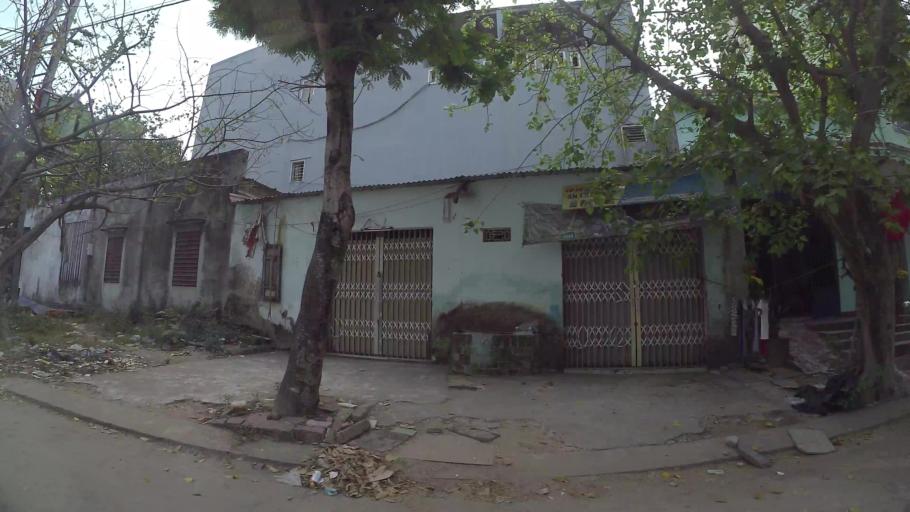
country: VN
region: Da Nang
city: Son Tra
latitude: 16.0890
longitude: 108.2471
